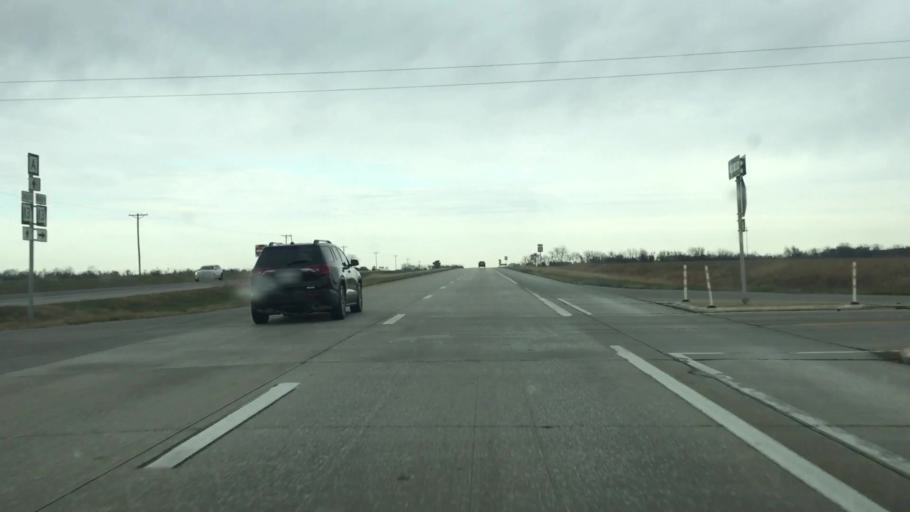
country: US
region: Missouri
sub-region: Saint Clair County
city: Osceola
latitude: 38.1517
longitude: -93.7228
